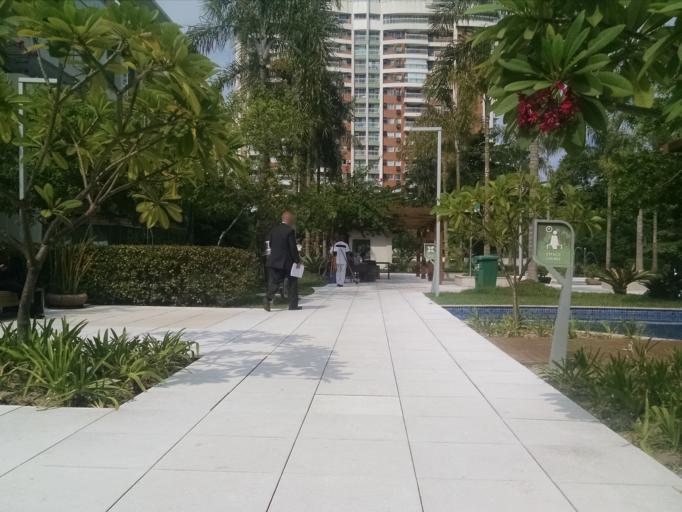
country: BR
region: Rio de Janeiro
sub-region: Rio De Janeiro
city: Rio de Janeiro
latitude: -22.9895
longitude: -43.3593
